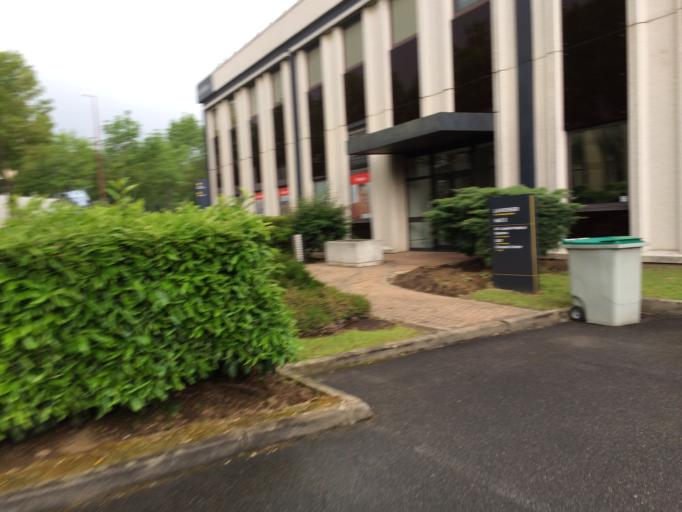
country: FR
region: Ile-de-France
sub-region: Departement de l'Essonne
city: Wissous
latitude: 48.7310
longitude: 2.3120
